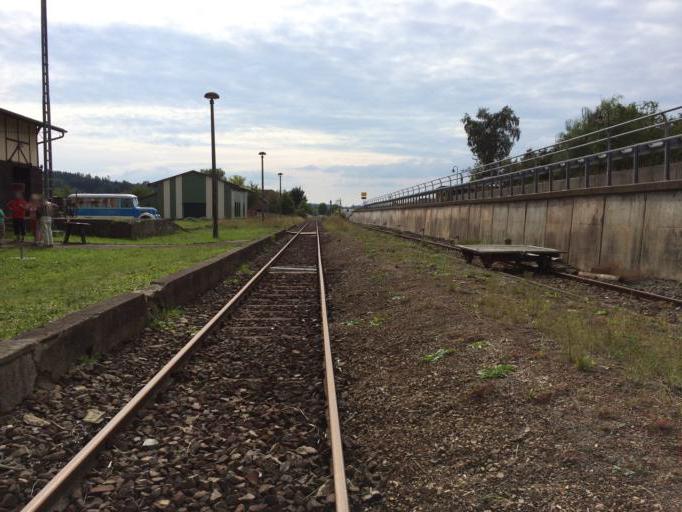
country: DE
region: Thuringia
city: Knau
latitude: 50.6548
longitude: 11.7144
